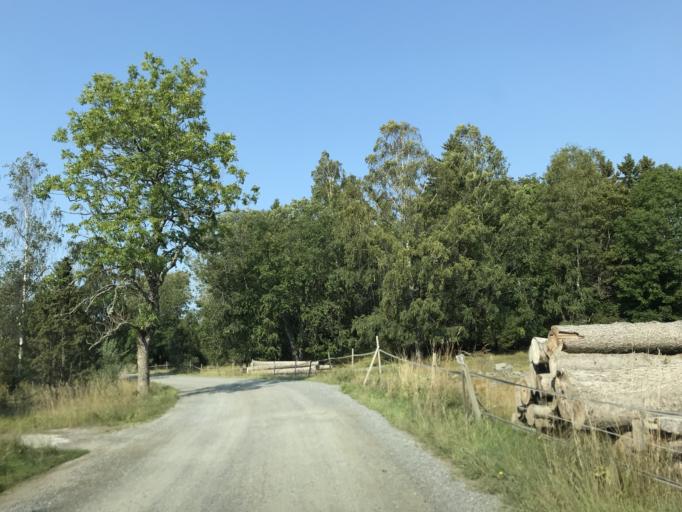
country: SE
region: Stockholm
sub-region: Norrtalje Kommun
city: Bjorko
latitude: 59.8488
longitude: 19.0143
